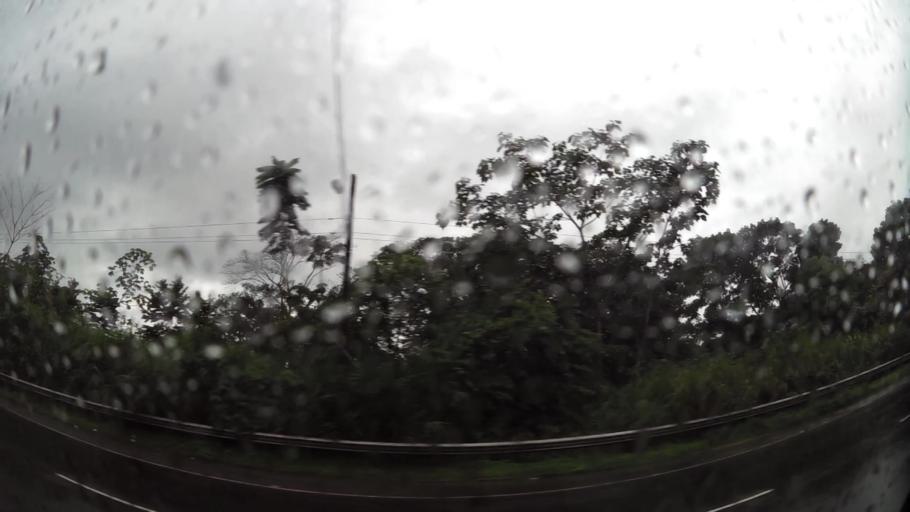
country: PA
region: Colon
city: Quebrada Bonita Adentro
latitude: 9.2845
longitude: -79.7136
